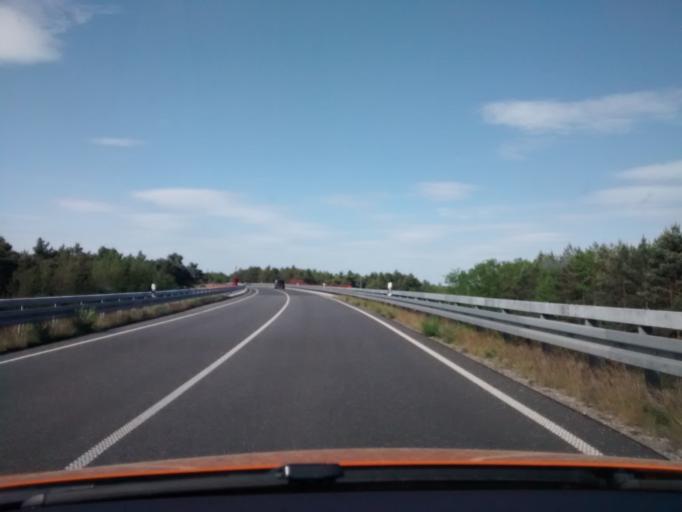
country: DE
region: Brandenburg
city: Luckenwalde
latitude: 52.0717
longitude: 13.1307
